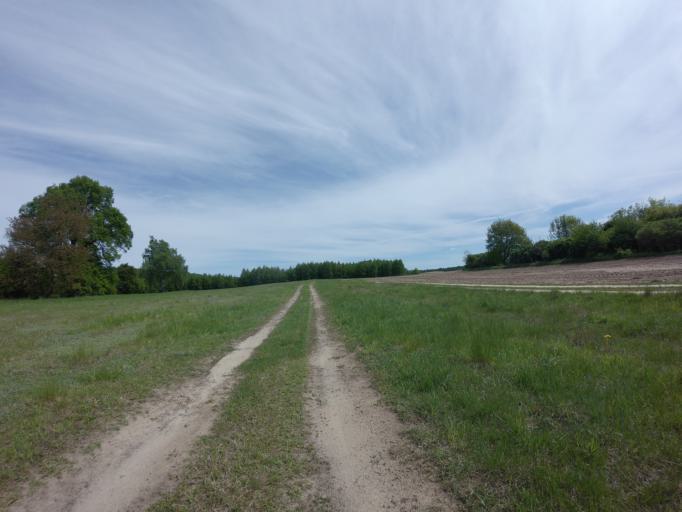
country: PL
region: West Pomeranian Voivodeship
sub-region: Powiat choszczenski
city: Recz
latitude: 53.1596
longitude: 15.5732
